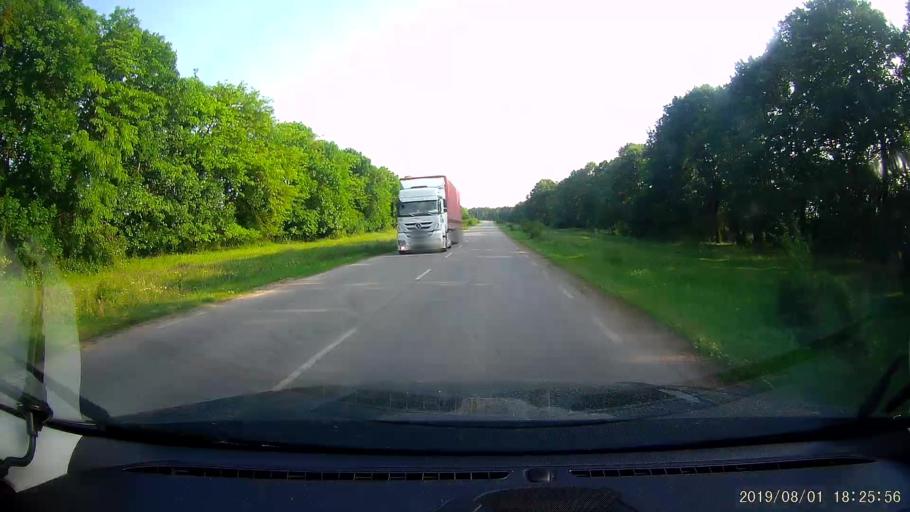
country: BG
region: Shumen
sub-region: Obshtina Venets
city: Venets
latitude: 43.6103
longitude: 26.9951
